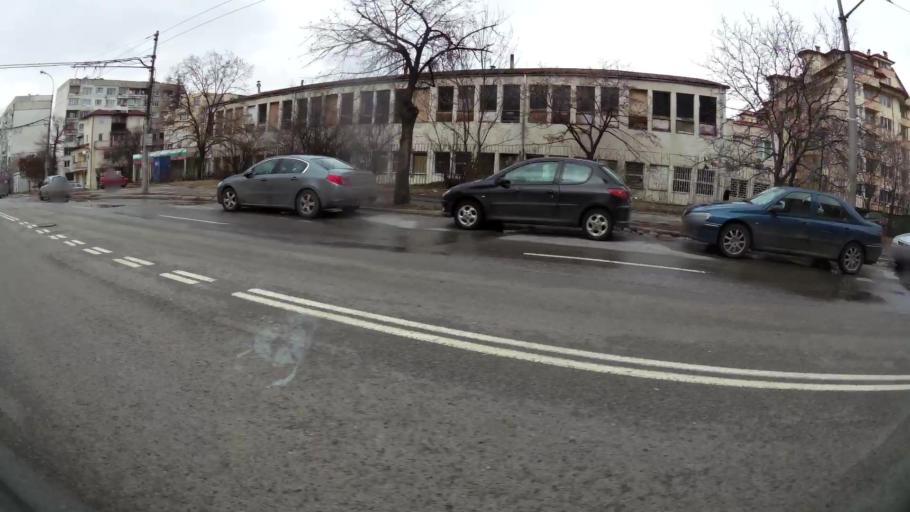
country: BG
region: Sofiya
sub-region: Obshtina Bozhurishte
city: Bozhurishte
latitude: 42.7241
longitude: 23.2575
